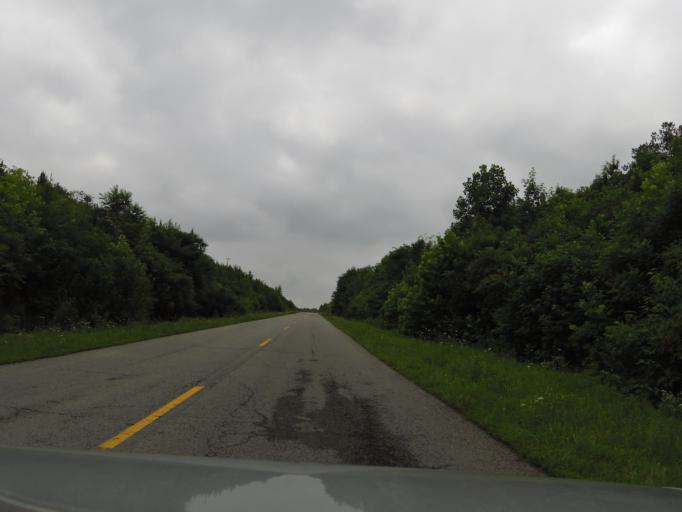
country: US
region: Kentucky
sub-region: Muhlenberg County
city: Morehead
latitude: 37.2785
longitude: -87.2980
